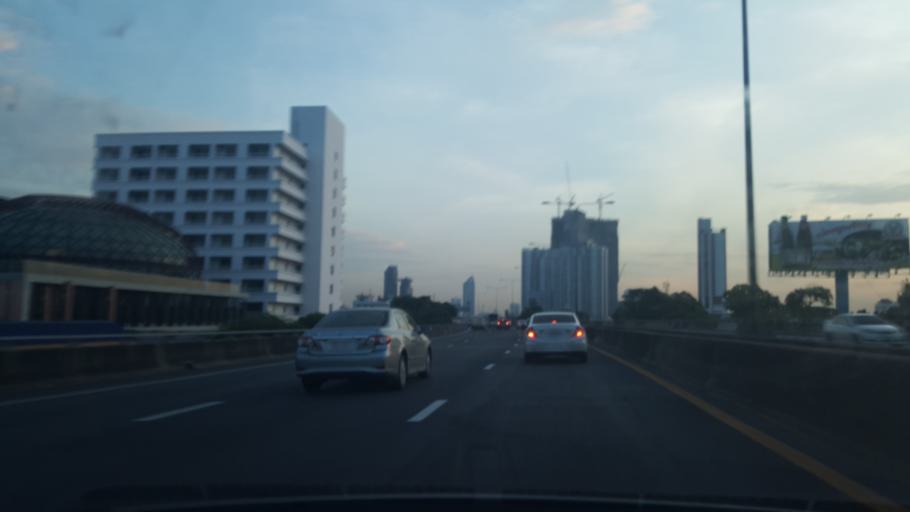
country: TH
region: Bangkok
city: Sathon
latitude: 13.7076
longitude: 100.5187
